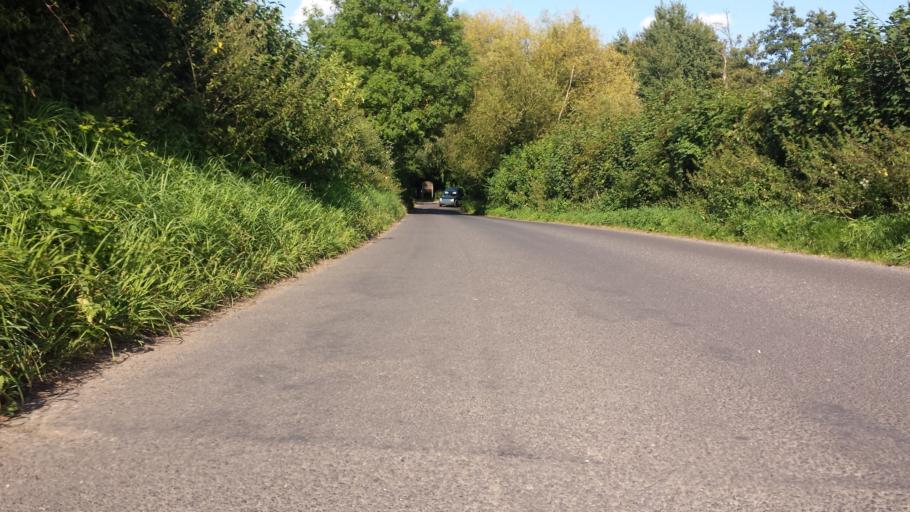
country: GB
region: England
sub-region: Kent
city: Shoreham
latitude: 51.3519
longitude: 0.1898
